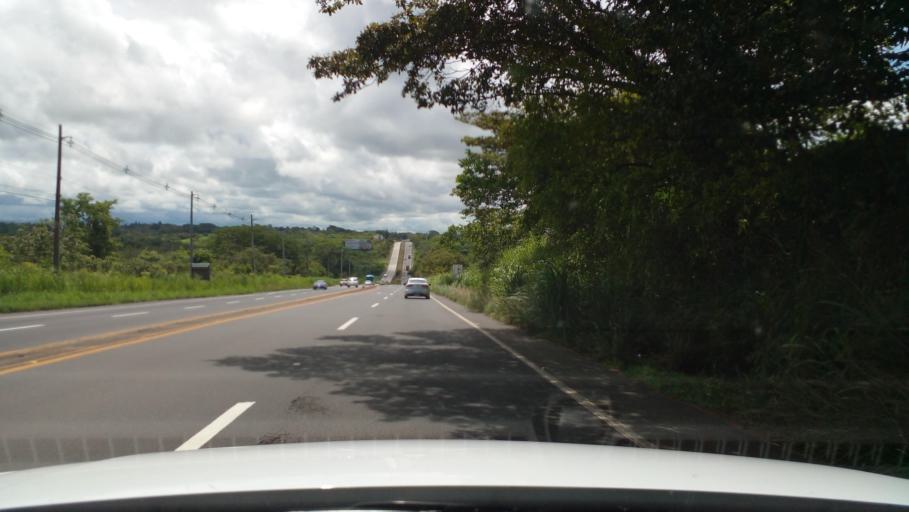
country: PA
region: Cocle
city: Rio Hato
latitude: 8.4278
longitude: -80.0698
